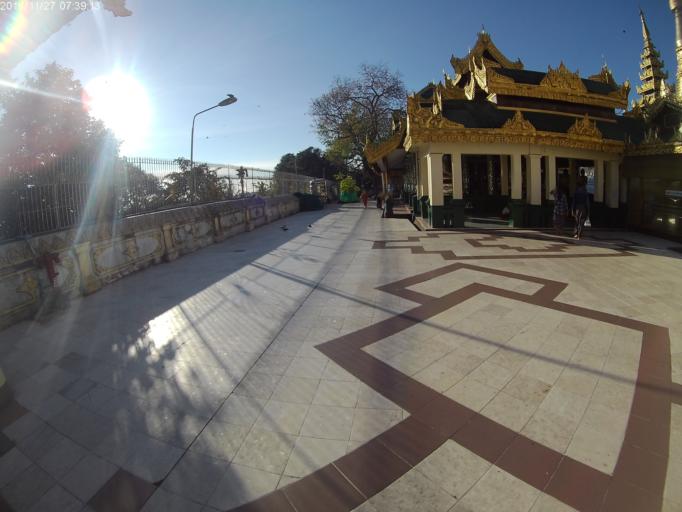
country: MM
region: Yangon
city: Yangon
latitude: 16.7978
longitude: 96.1507
